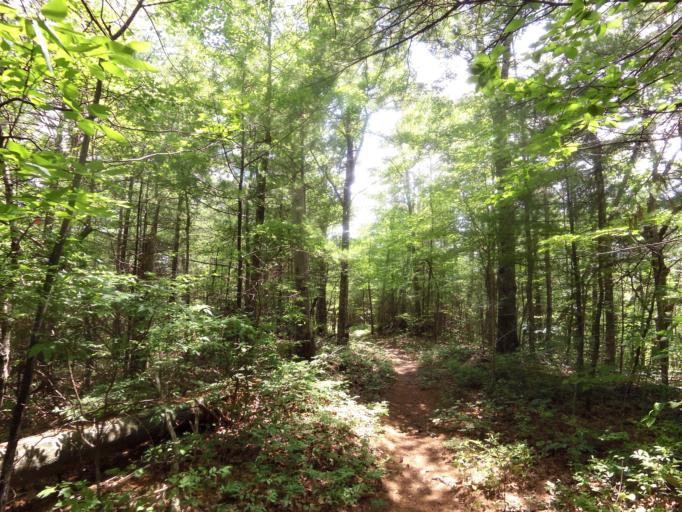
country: US
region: Tennessee
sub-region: Blount County
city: Wildwood
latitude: 35.6707
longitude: -83.8354
